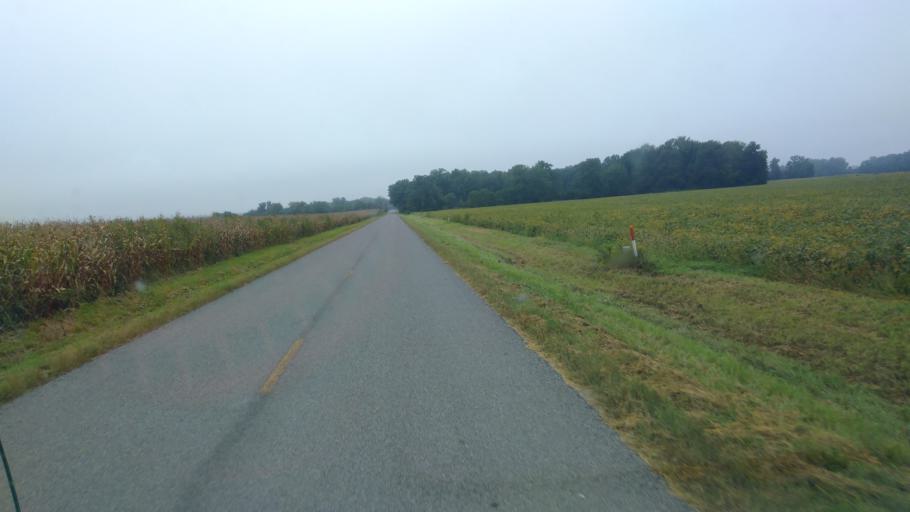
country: US
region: Ohio
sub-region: Logan County
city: Northwood
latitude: 40.4717
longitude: -83.6068
